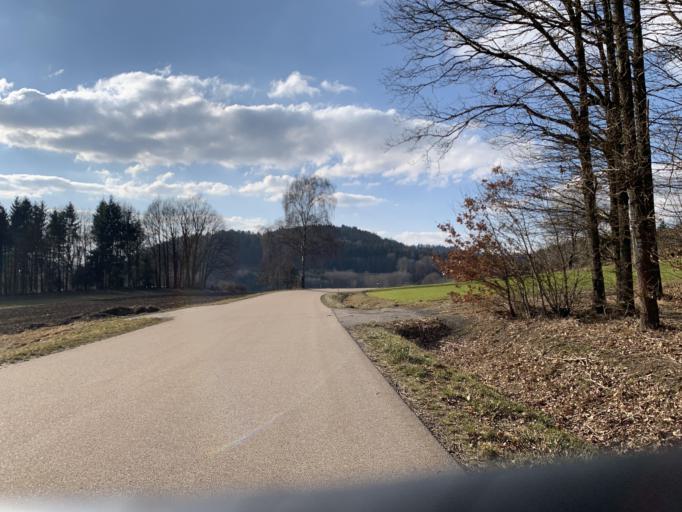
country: DE
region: Bavaria
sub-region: Upper Palatinate
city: Thanstein
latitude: 49.3811
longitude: 12.4603
